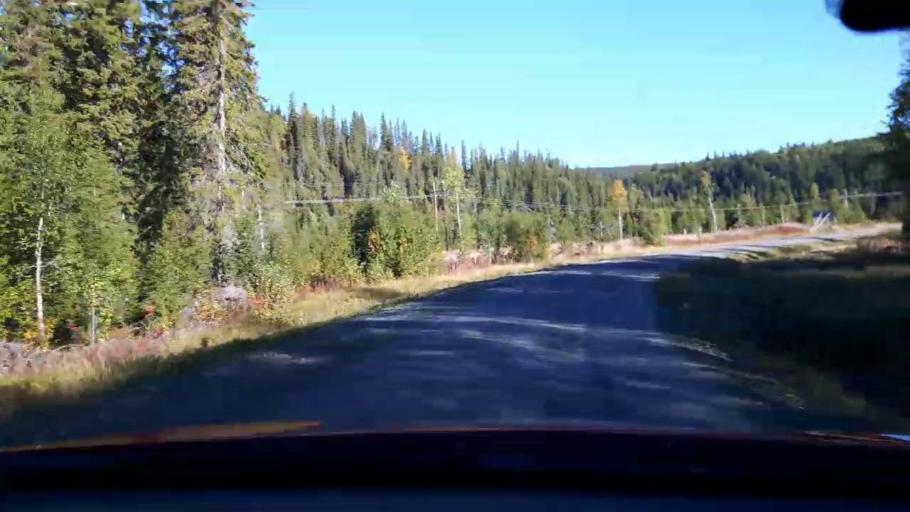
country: NO
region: Nord-Trondelag
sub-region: Lierne
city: Sandvika
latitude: 64.6478
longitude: 13.7462
